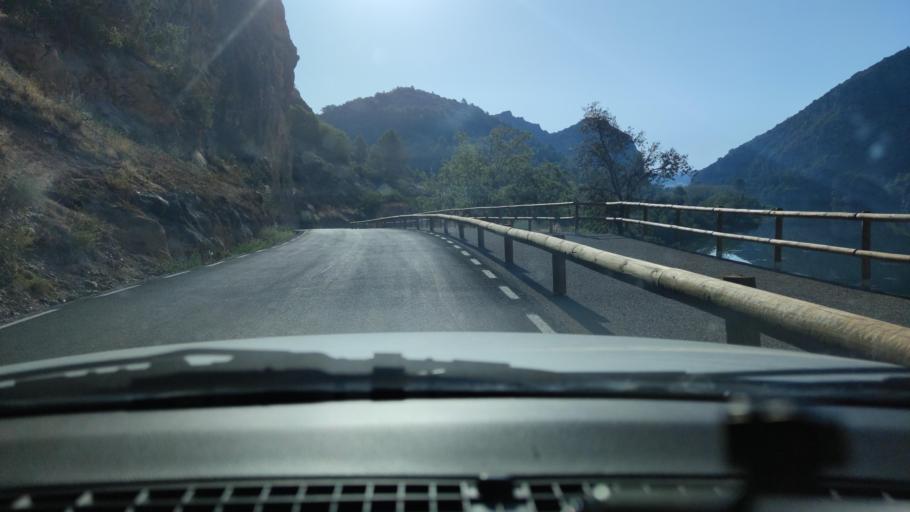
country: ES
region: Catalonia
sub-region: Provincia de Lleida
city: Camarasa
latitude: 41.8743
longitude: 0.8482
